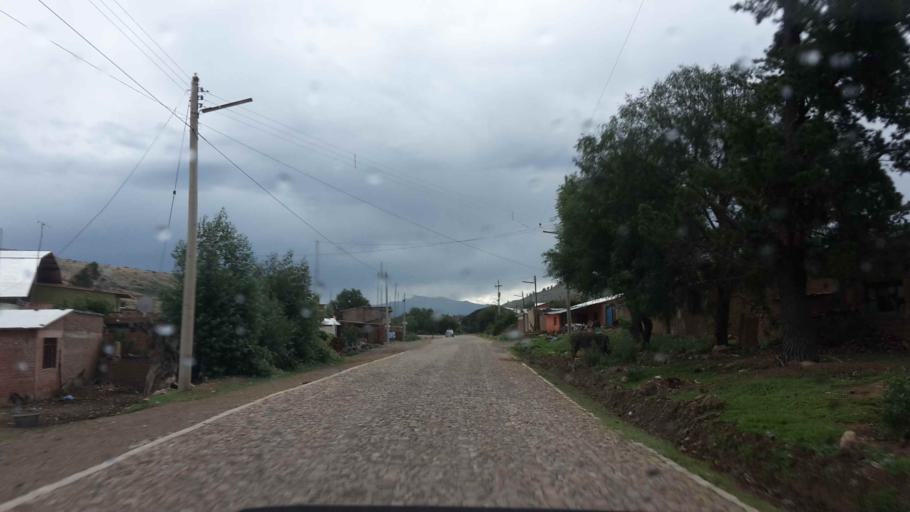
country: BO
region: Cochabamba
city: Cochabamba
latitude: -17.5492
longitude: -66.1773
